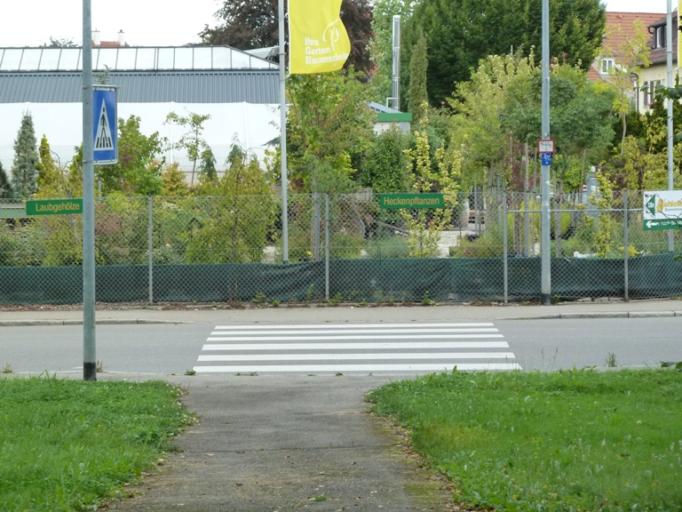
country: DE
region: Baden-Wuerttemberg
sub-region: Tuebingen Region
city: Reutlingen
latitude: 48.4965
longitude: 9.1759
